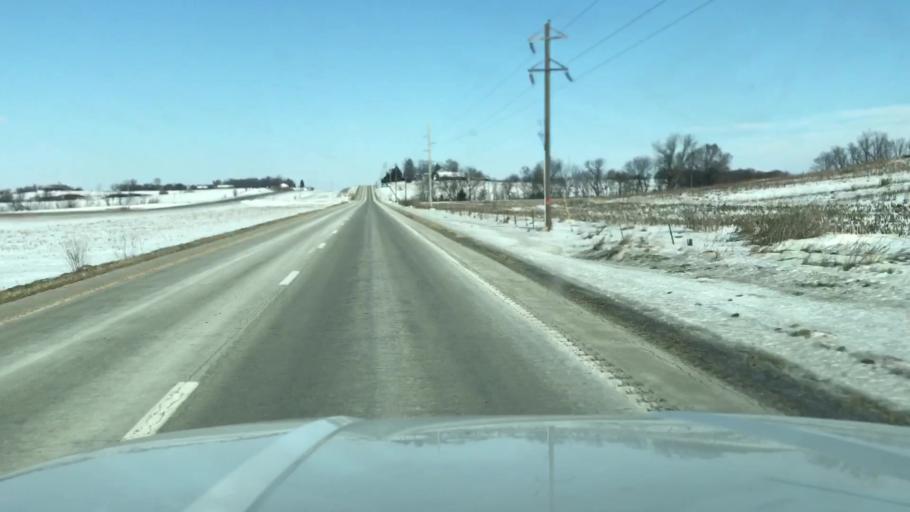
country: US
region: Missouri
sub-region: Nodaway County
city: Maryville
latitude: 40.1463
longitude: -94.8692
